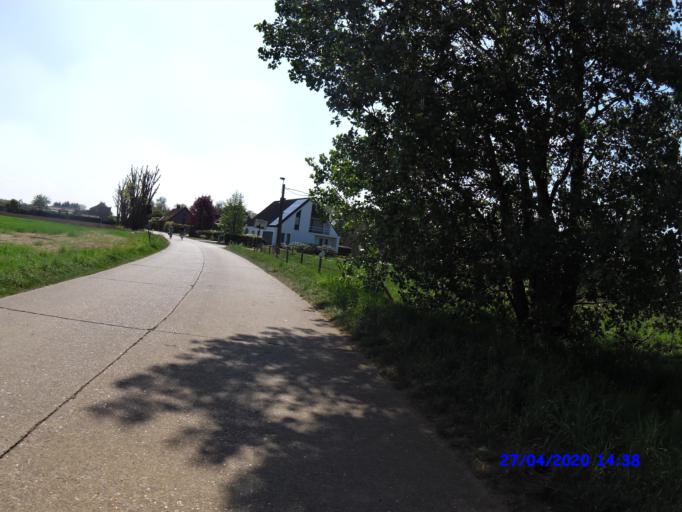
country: BE
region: Flanders
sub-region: Provincie Antwerpen
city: Lille
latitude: 51.2303
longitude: 4.8472
